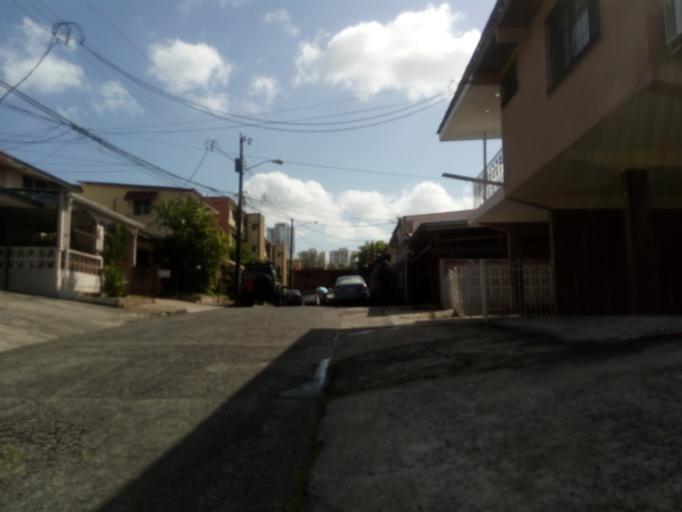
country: PA
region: Panama
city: Panama
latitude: 8.9933
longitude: -79.5390
